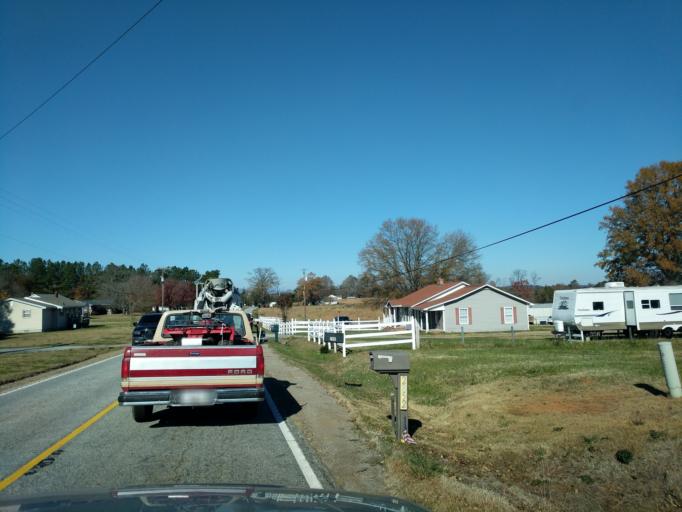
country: US
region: South Carolina
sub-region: Spartanburg County
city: Duncan
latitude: 35.0108
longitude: -82.1804
